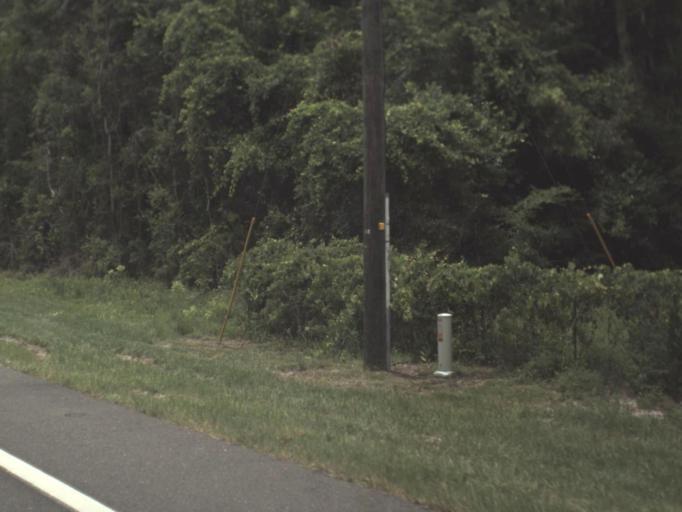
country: US
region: Florida
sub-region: Levy County
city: Manatee Road
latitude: 29.4964
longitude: -82.9202
